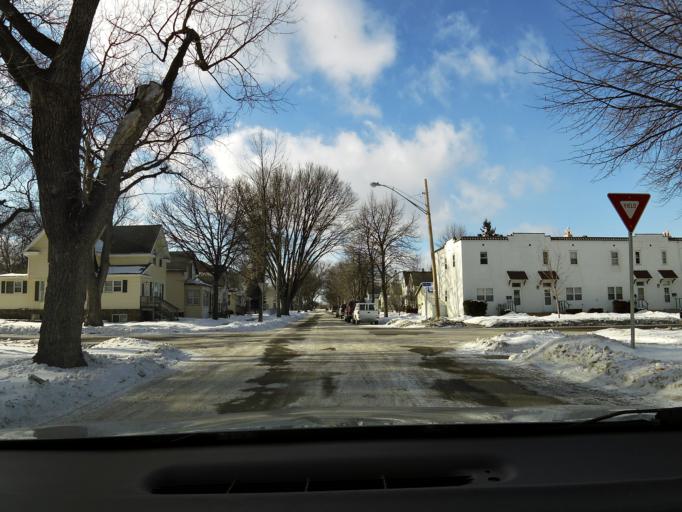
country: US
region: North Dakota
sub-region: Grand Forks County
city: Grand Forks
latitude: 47.9253
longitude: -97.0402
